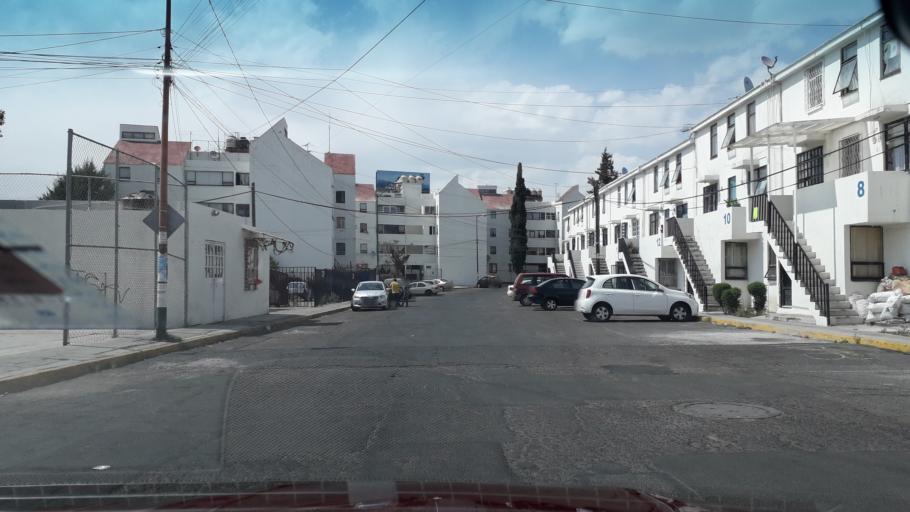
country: MX
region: Puebla
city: Puebla
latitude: 19.0393
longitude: -98.2201
